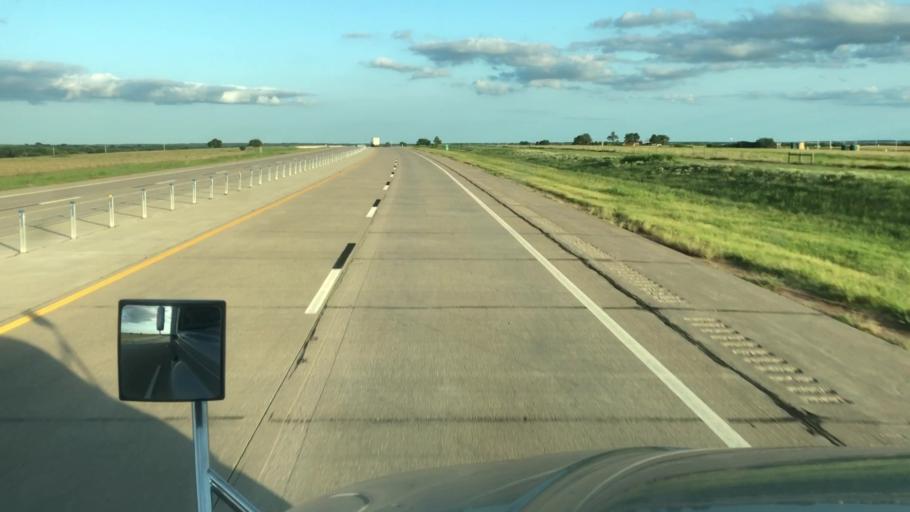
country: US
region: Oklahoma
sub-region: Pawnee County
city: Pawnee
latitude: 36.3392
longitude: -97.0222
